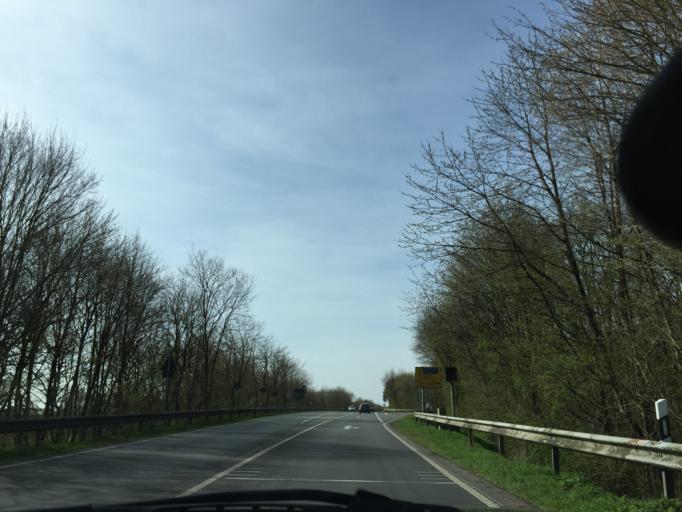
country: DE
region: North Rhine-Westphalia
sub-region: Regierungsbezirk Dusseldorf
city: Goch
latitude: 51.6892
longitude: 6.1317
